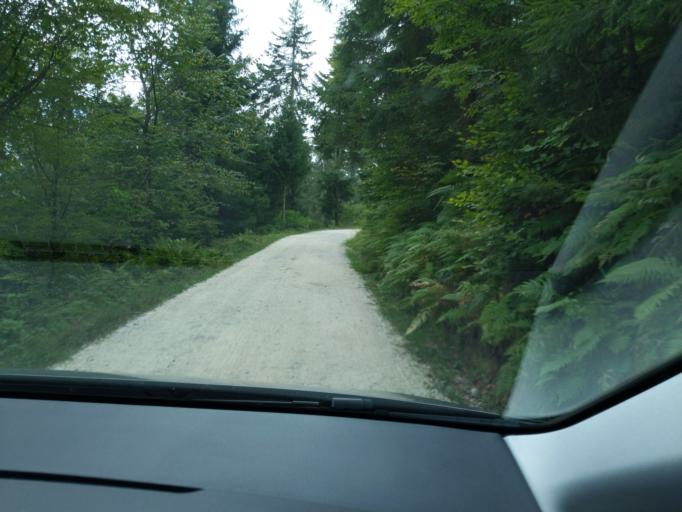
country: CH
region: Bern
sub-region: Oberaargau
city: Wyssachen
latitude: 47.0364
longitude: 7.8291
